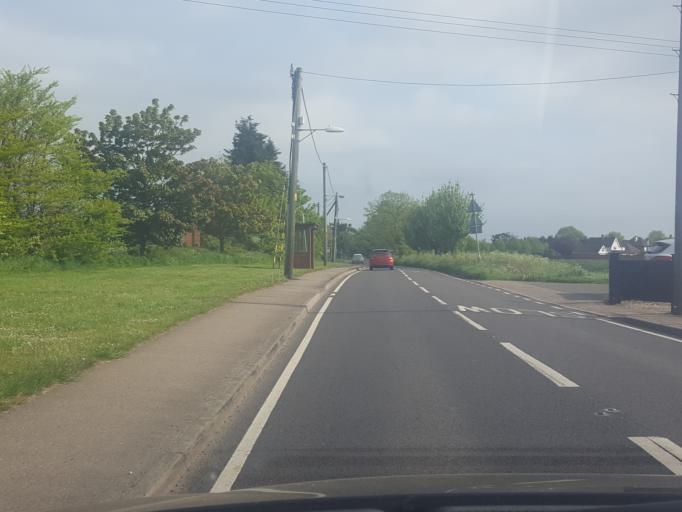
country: GB
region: England
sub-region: Essex
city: Frinton-on-Sea
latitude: 51.8319
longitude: 1.2093
